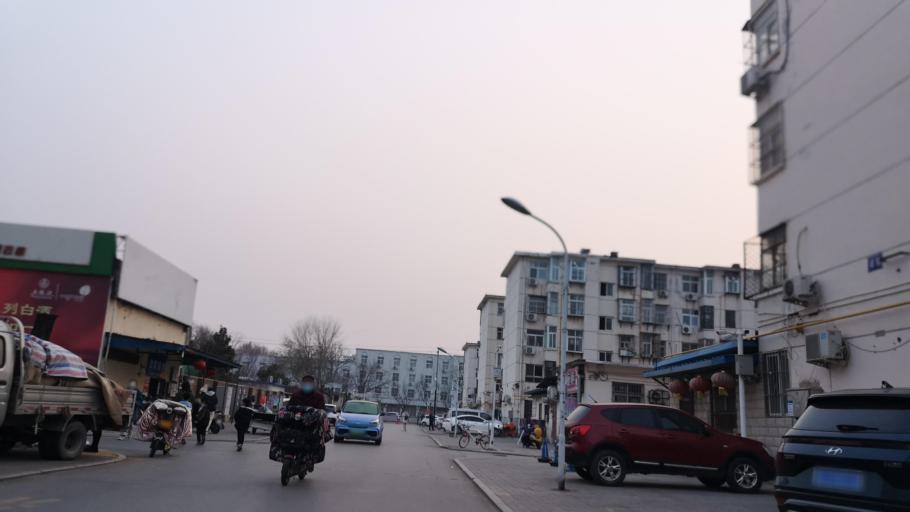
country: CN
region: Henan Sheng
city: Zhongyuanlu
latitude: 35.7814
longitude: 115.0748
